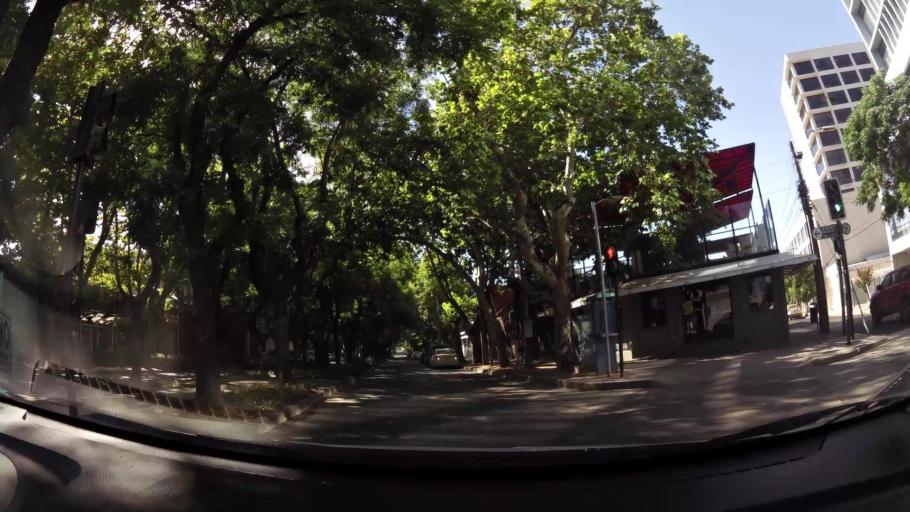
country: CL
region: Maule
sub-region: Provincia de Talca
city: Talca
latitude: -35.4257
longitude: -71.6667
